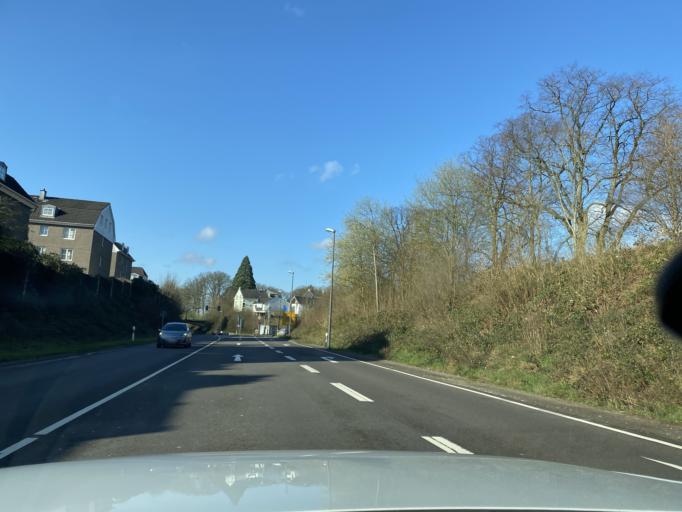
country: DE
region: North Rhine-Westphalia
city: Wermelskirchen
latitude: 51.1359
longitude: 7.2051
